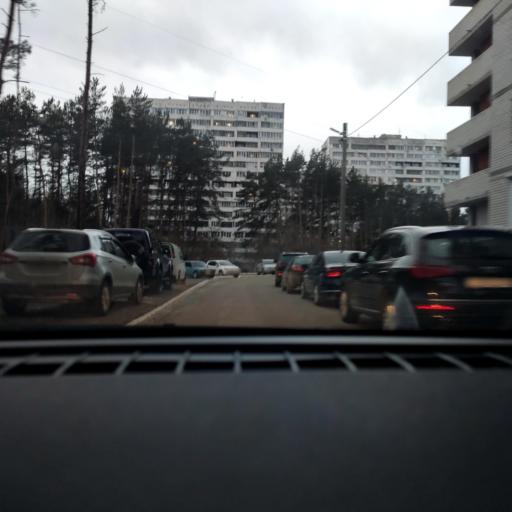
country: RU
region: Voronezj
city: Pridonskoy
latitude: 51.6526
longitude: 39.1156
